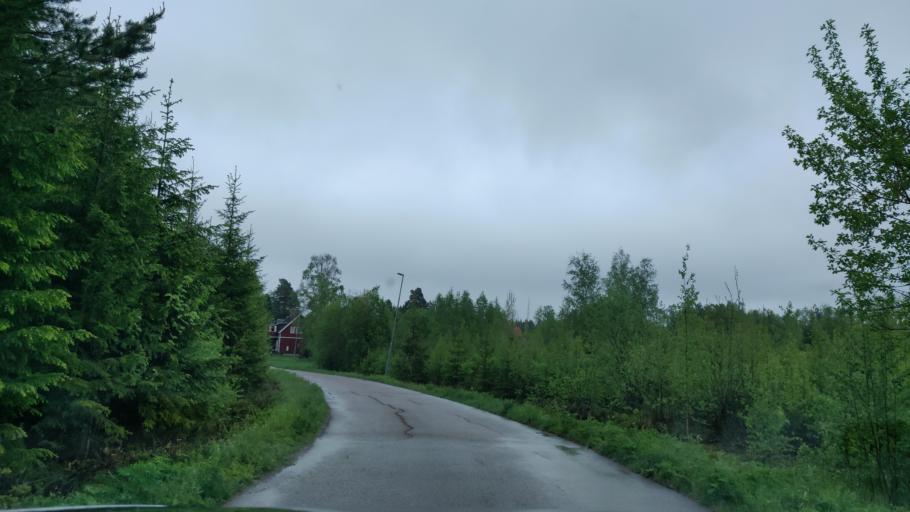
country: SE
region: Dalarna
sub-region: Avesta Kommun
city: Horndal
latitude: 60.3042
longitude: 16.4061
